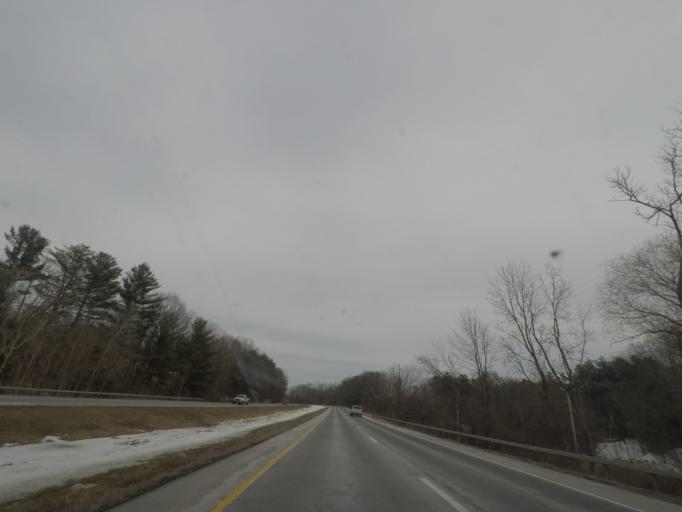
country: US
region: New York
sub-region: Albany County
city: Delmar
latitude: 42.6052
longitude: -73.8291
